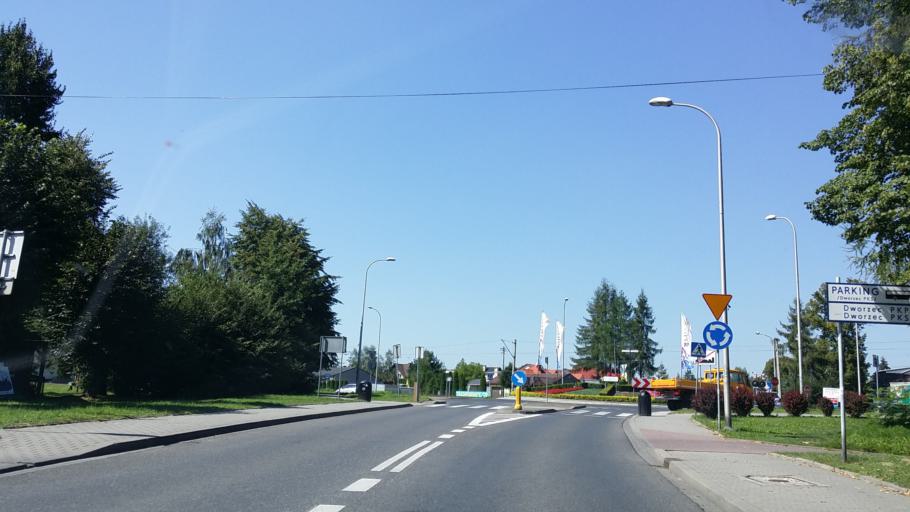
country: PL
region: Lesser Poland Voivodeship
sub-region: Powiat wadowicki
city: Tomice
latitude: 49.8869
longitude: 19.4818
